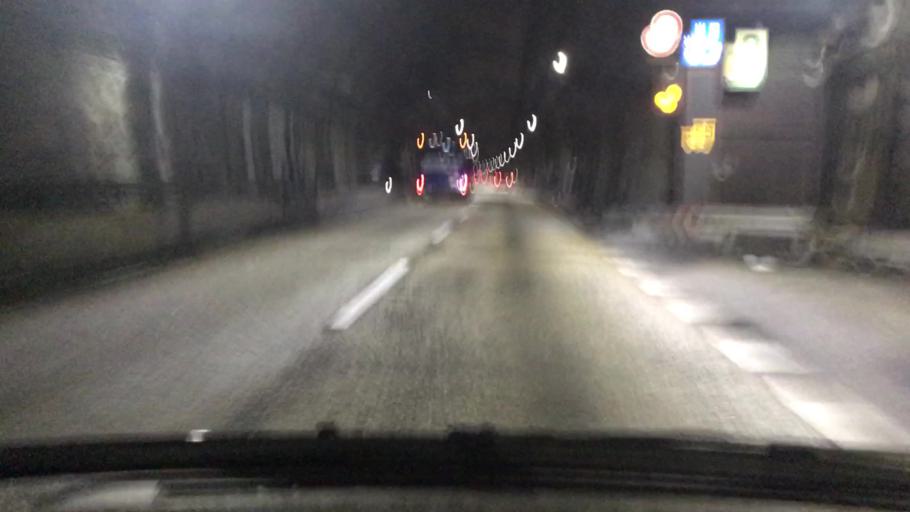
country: JP
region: Hyogo
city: Kobe
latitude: 34.7111
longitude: 135.1922
